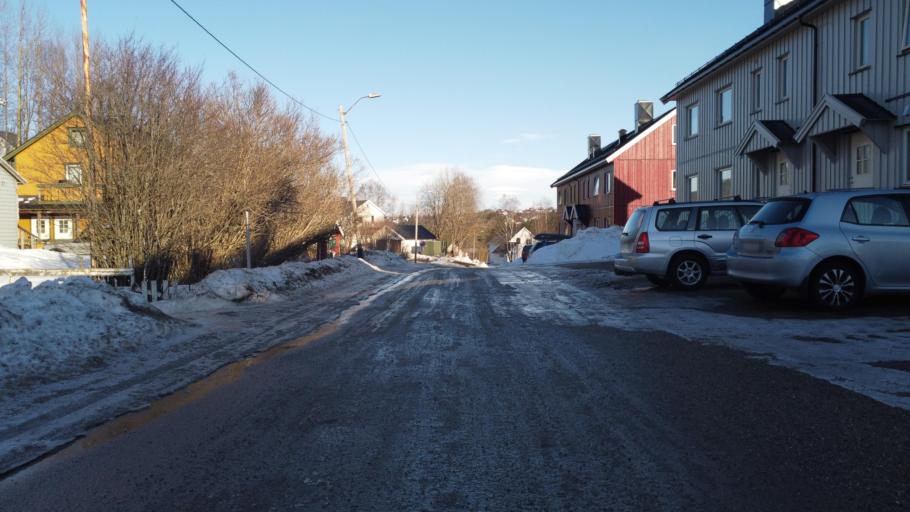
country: NO
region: Nordland
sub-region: Rana
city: Mo i Rana
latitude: 66.3160
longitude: 14.1629
